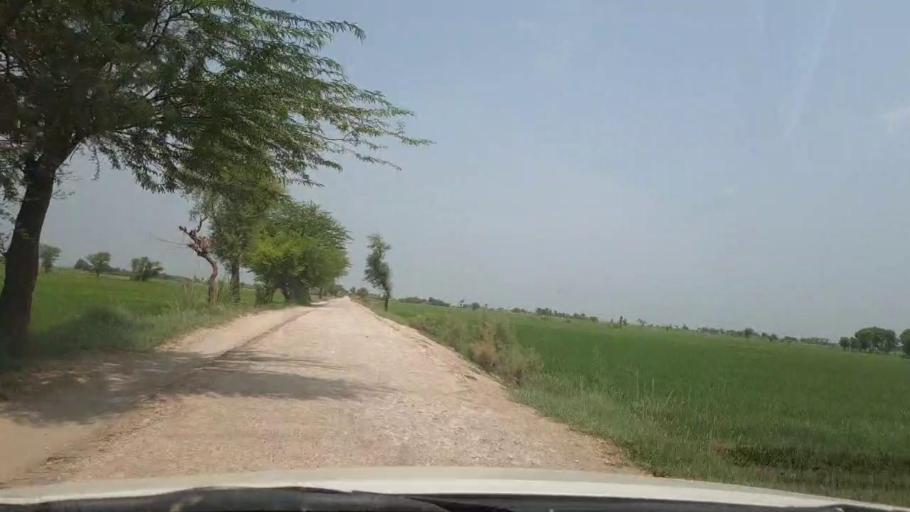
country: PK
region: Sindh
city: Rustam jo Goth
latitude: 28.0352
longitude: 68.8140
